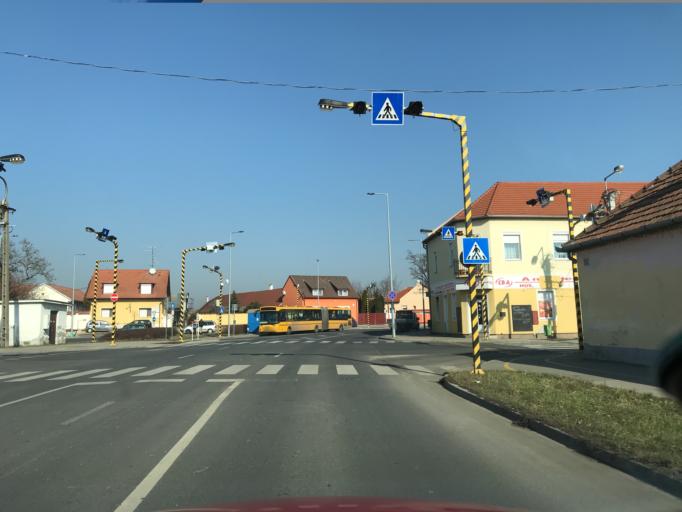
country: HU
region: Gyor-Moson-Sopron
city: Gyor
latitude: 47.6818
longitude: 17.6110
